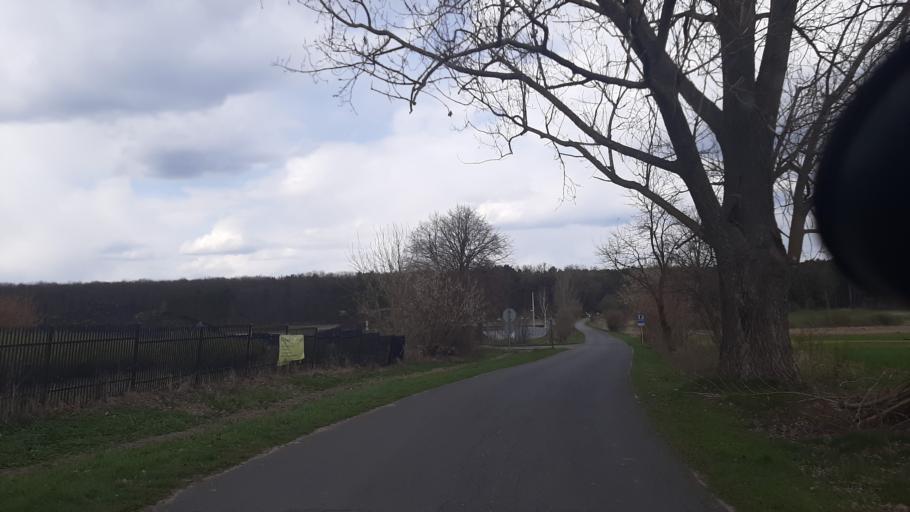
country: PL
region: Lublin Voivodeship
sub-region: Powiat lubelski
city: Niemce
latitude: 51.3651
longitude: 22.5528
